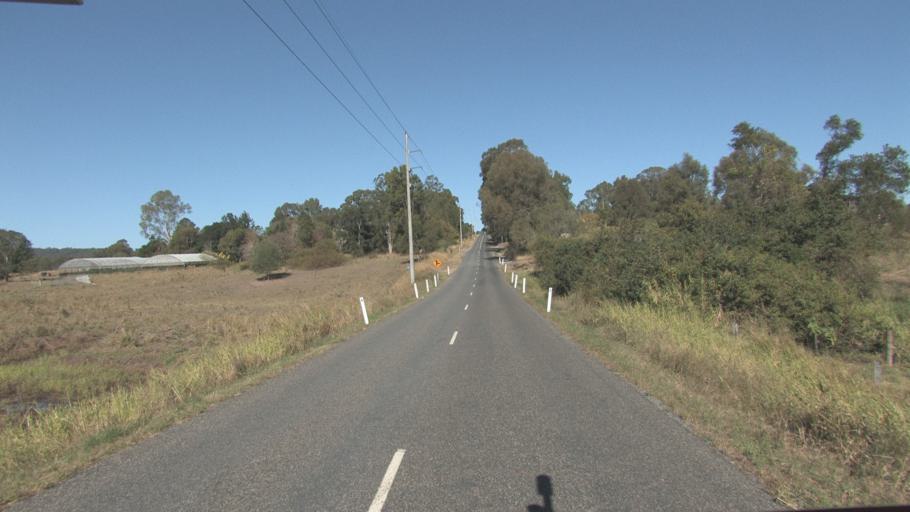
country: AU
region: Queensland
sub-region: Logan
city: Cedar Vale
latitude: -27.8734
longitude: 153.0170
